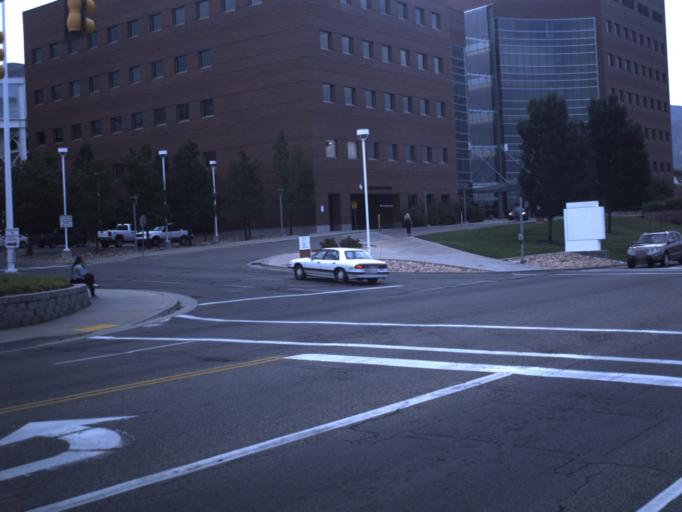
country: US
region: Utah
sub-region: Salt Lake County
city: Salt Lake City
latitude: 40.7701
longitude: -111.8392
